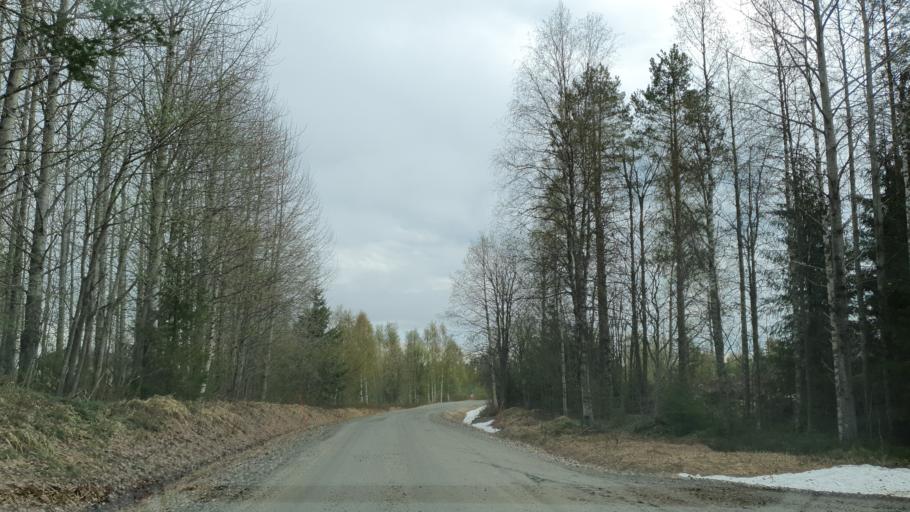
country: FI
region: Kainuu
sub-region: Kehys-Kainuu
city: Kuhmo
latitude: 64.1395
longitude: 29.9675
